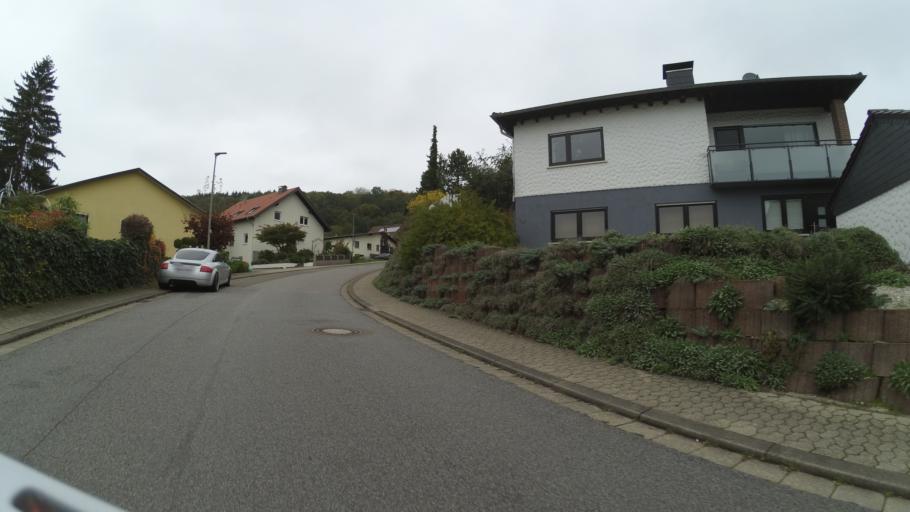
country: DE
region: Saarland
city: Blieskastel
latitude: 49.2630
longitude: 7.2766
